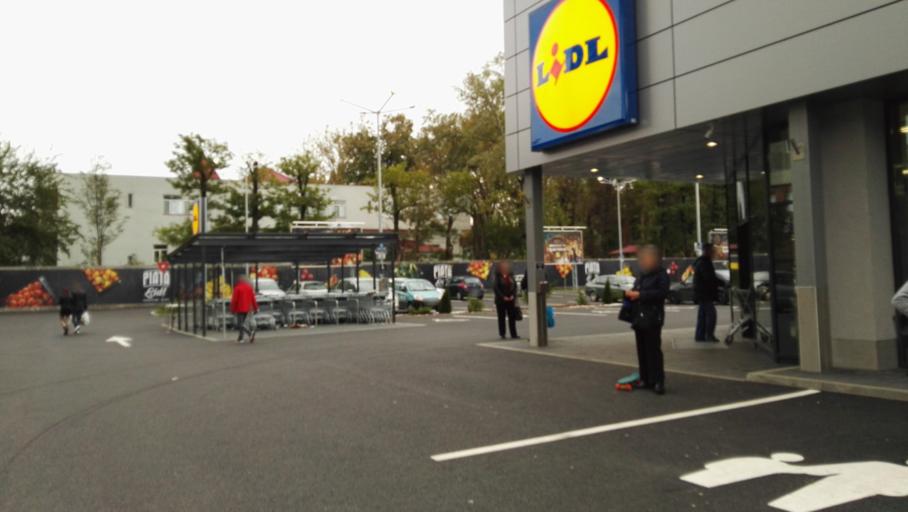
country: RO
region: Ilfov
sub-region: Comuna Popesti-Leordeni
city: Popesti-Leordeni
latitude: 44.3889
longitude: 26.1250
